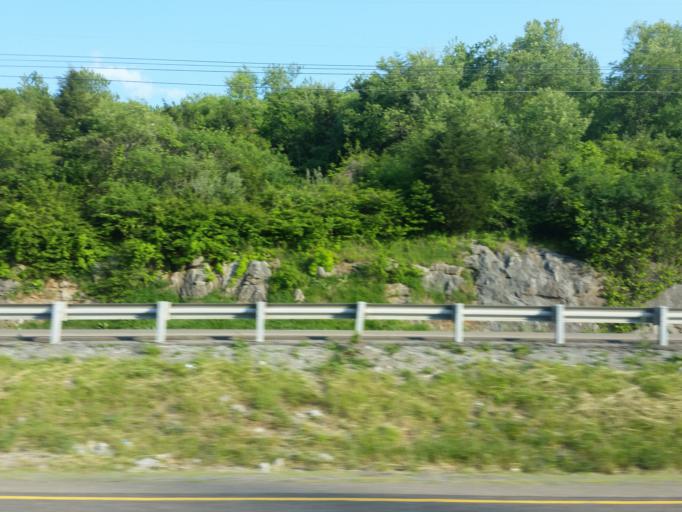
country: US
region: Virginia
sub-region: Tazewell County
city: Claypool Hill
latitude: 37.0042
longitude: -81.8084
